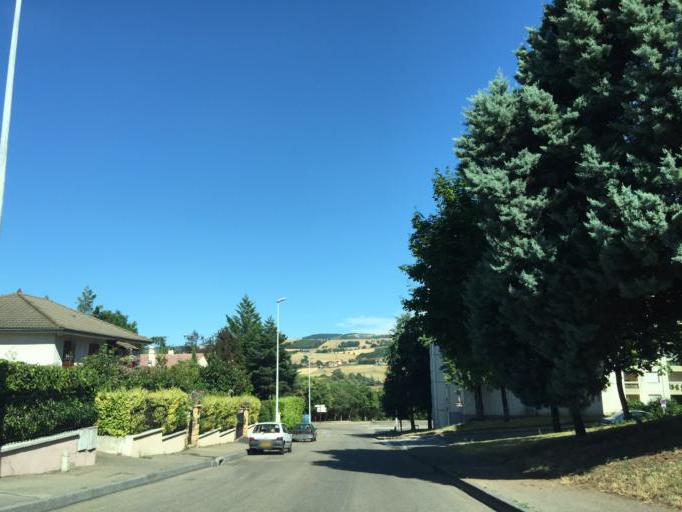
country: FR
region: Rhone-Alpes
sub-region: Departement de la Loire
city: Saint-Chamond
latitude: 45.4774
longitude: 4.5354
